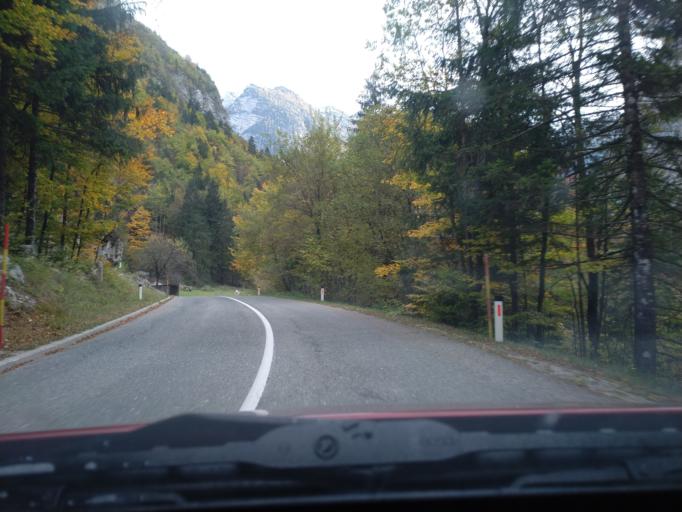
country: SI
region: Kranjska Gora
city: Kranjska Gora
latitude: 46.3941
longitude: 13.7440
